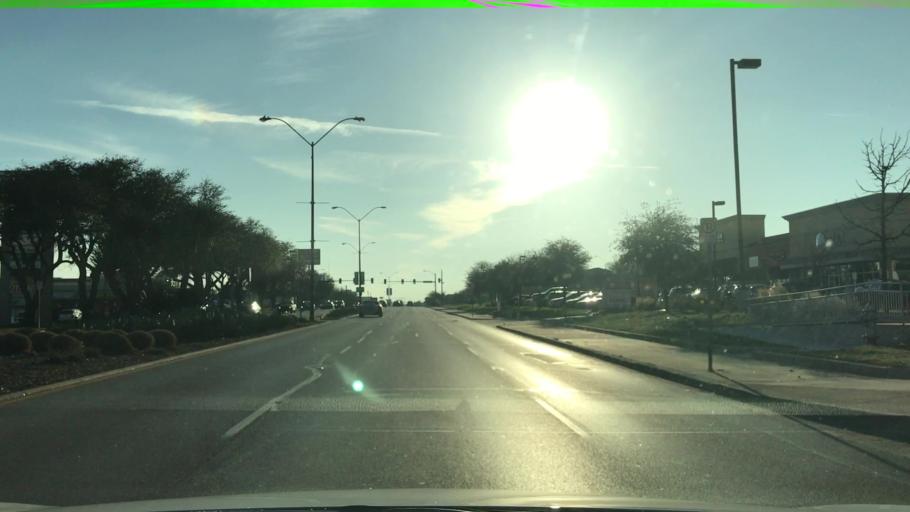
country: US
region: Texas
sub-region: Tarrant County
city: Westworth
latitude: 32.7266
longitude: -97.4207
